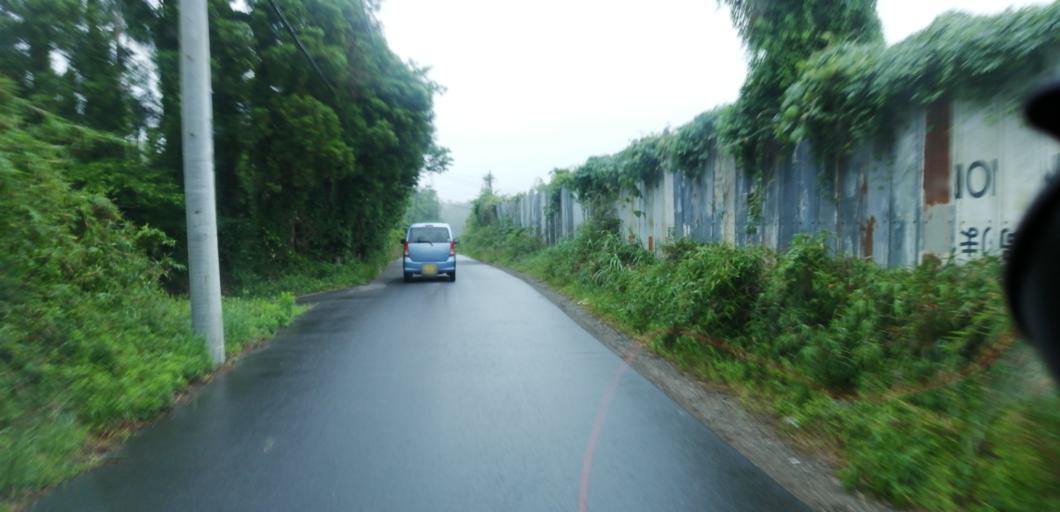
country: JP
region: Chiba
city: Ichihara
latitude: 35.4794
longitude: 140.1500
